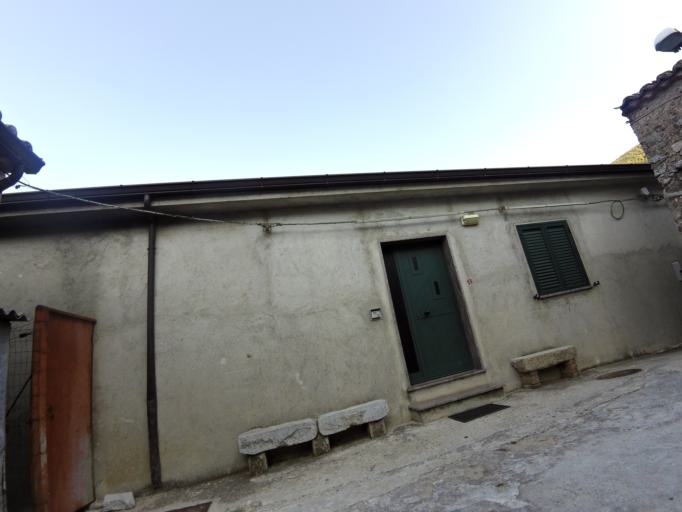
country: IT
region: Calabria
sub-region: Provincia di Vibo-Valentia
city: Nardodipace
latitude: 38.4409
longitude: 16.3441
